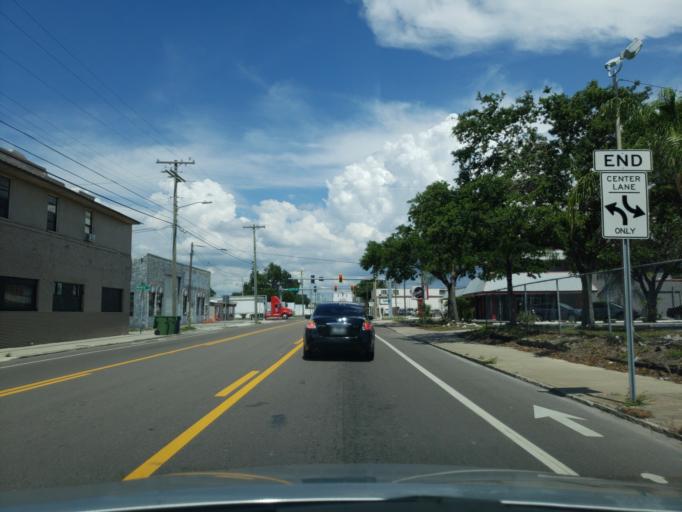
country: US
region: Florida
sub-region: Hillsborough County
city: Tampa
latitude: 27.9602
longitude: -82.4166
